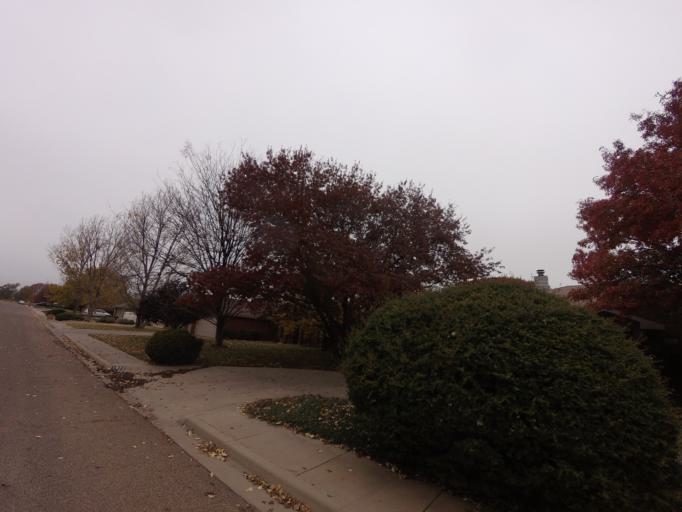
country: US
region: New Mexico
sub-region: Curry County
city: Clovis
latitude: 34.4271
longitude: -103.1841
